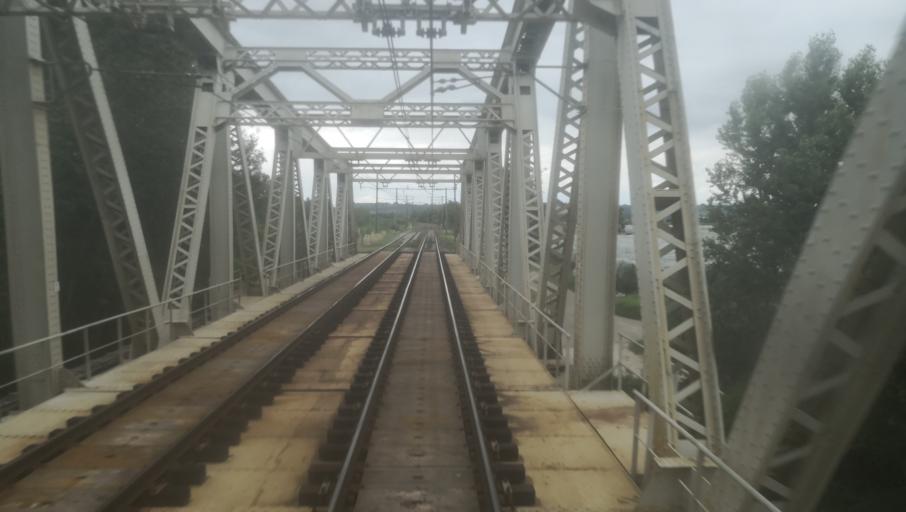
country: FR
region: Midi-Pyrenees
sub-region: Departement du Tarn-et-Garonne
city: Moissac
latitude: 44.0923
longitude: 1.1053
